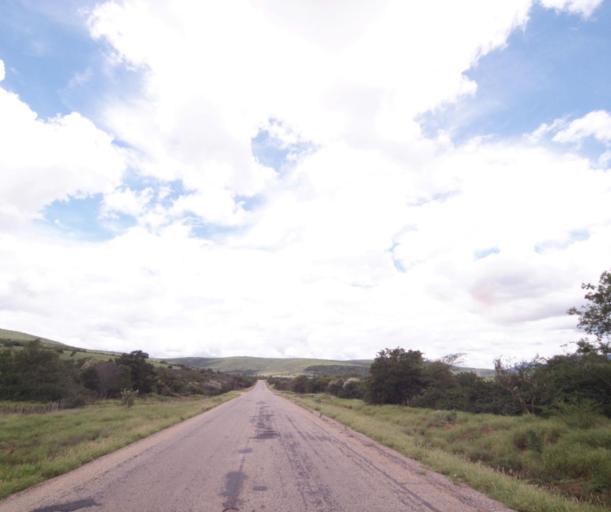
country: BR
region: Bahia
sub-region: Brumado
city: Brumado
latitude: -14.1898
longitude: -41.5769
